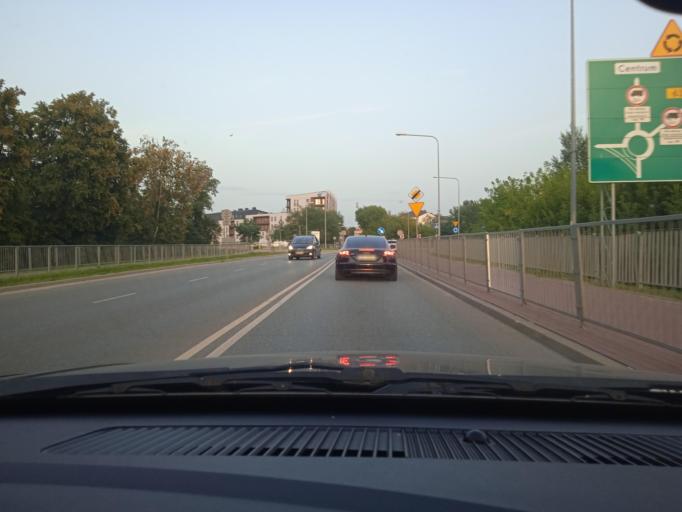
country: PL
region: Masovian Voivodeship
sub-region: Powiat nowodworski
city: Nowy Dwor Mazowiecki
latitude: 52.4317
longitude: 20.7029
